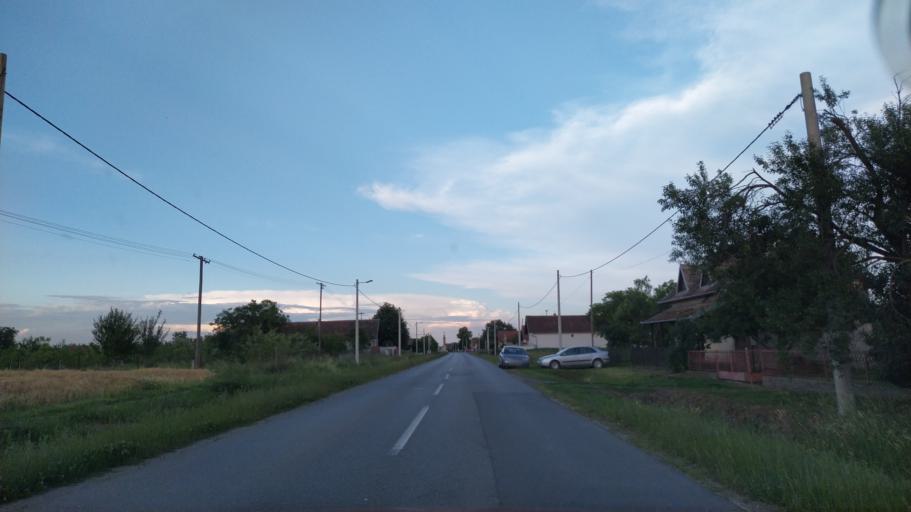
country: HR
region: Osjecko-Baranjska
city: Gorjani
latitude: 45.4607
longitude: 18.3108
